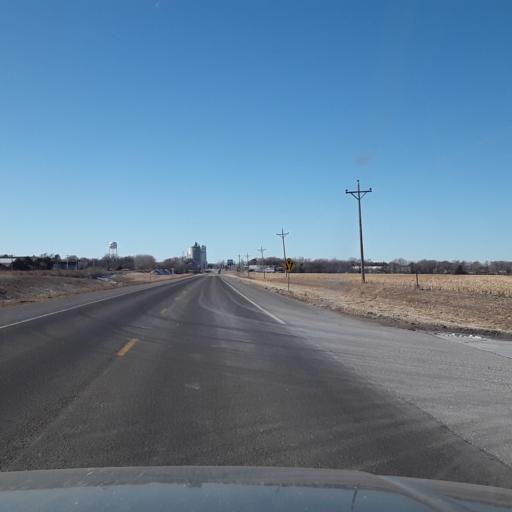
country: US
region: Nebraska
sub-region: Kearney County
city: Minden
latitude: 40.5073
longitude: -98.9341
